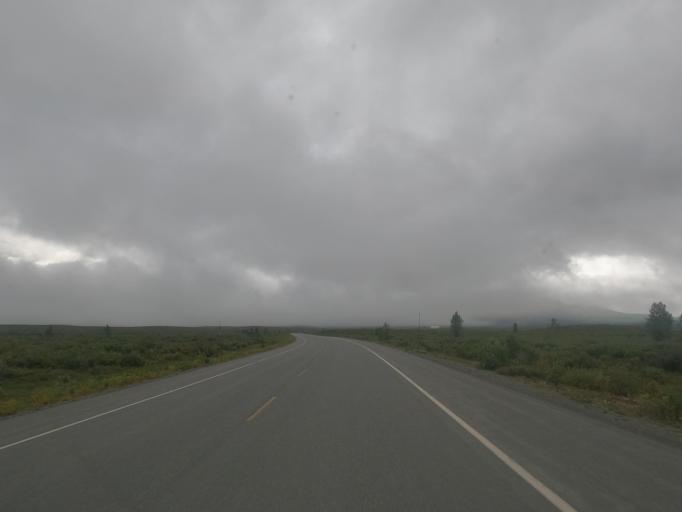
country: US
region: Alaska
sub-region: Haines Borough
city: Haines
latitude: 59.8007
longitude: -136.6160
